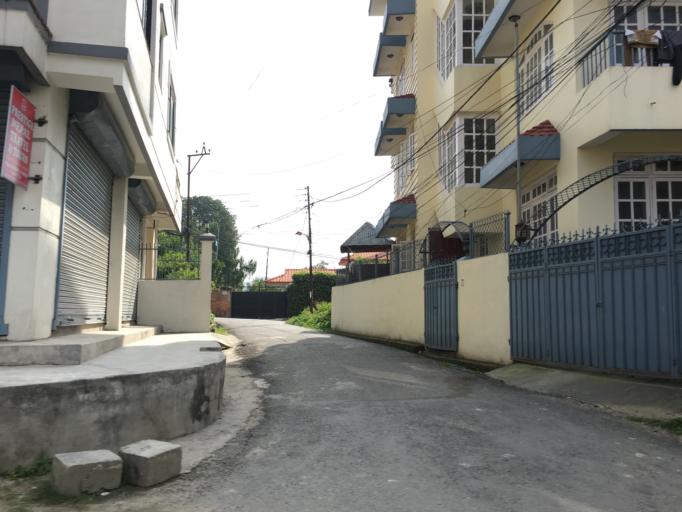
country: NP
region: Central Region
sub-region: Bagmati Zone
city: Kathmandu
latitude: 27.7442
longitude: 85.3474
